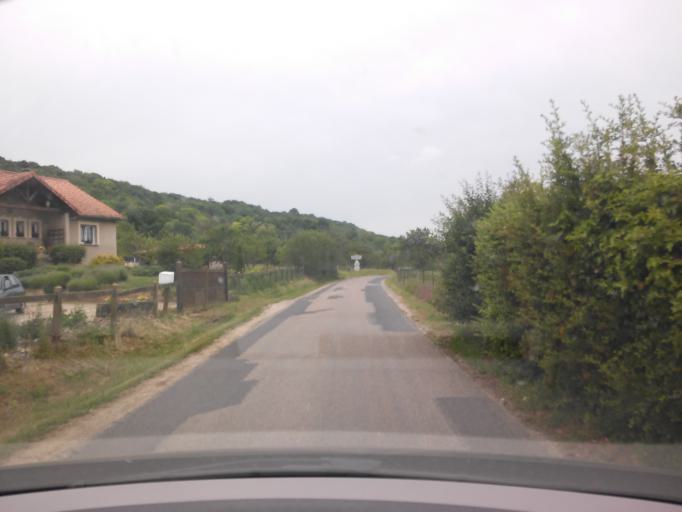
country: FR
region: Lorraine
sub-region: Departement de la Meuse
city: Vignot
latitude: 48.8003
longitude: 5.6518
